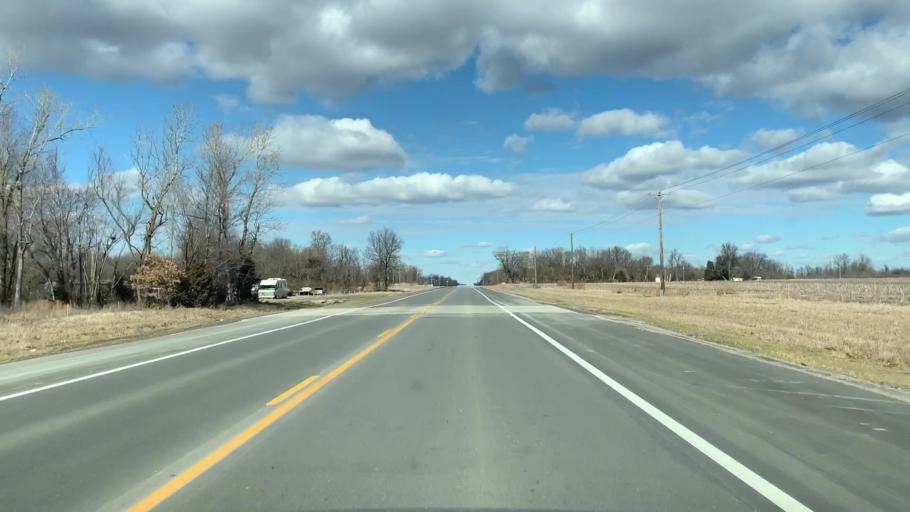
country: US
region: Kansas
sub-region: Cherokee County
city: Columbus
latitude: 37.2187
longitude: -94.8318
